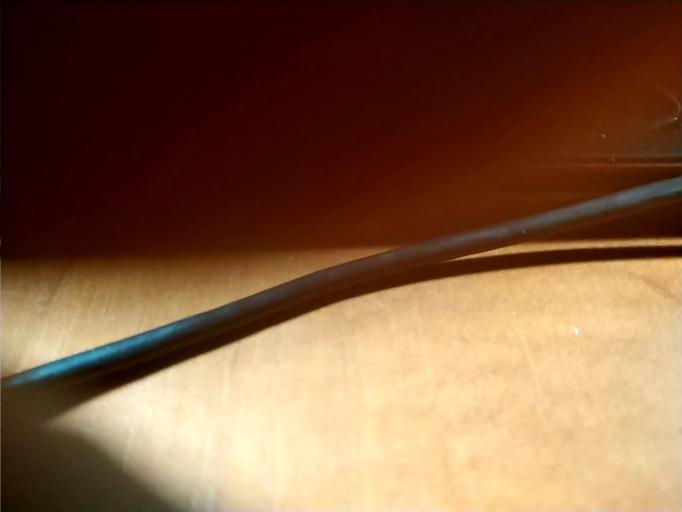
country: RU
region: Tverskaya
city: Sakharovo
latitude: 56.8128
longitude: 35.9940
